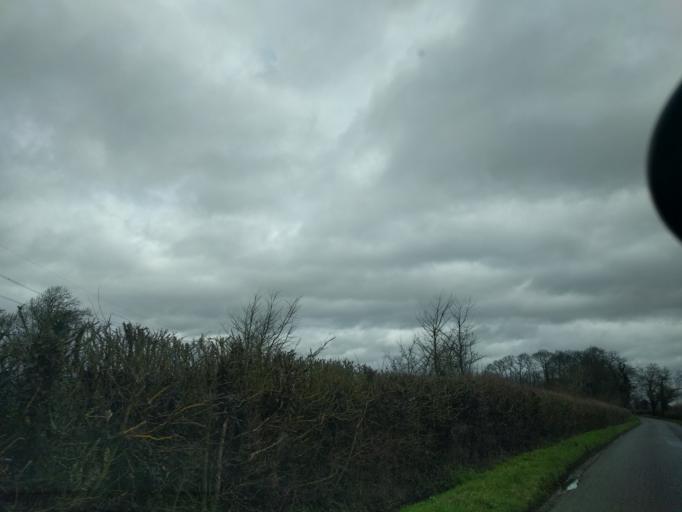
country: GB
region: England
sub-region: Wiltshire
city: Biddestone
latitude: 51.4779
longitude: -2.1957
